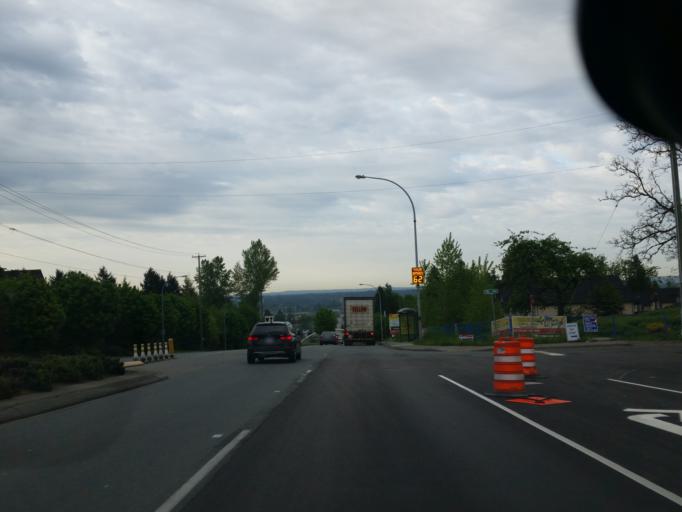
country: CA
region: British Columbia
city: Langley
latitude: 49.1302
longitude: -122.6685
